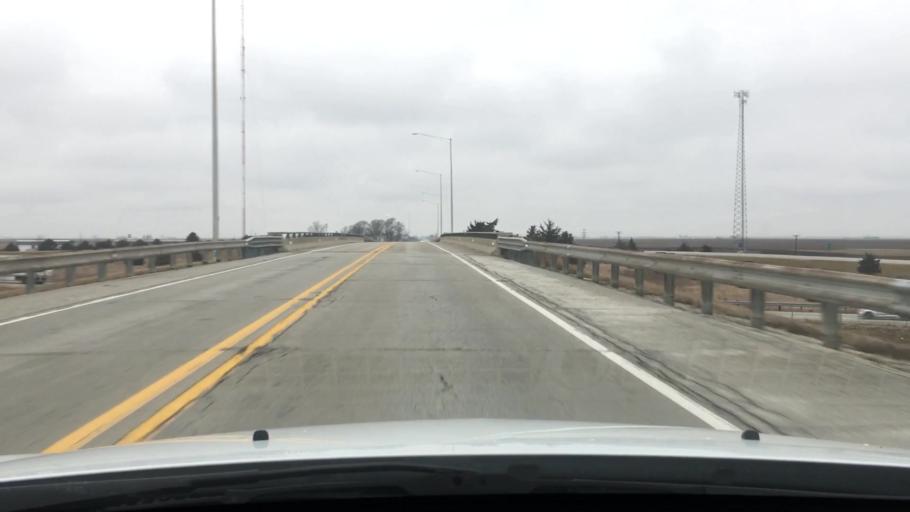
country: US
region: Illinois
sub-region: Iroquois County
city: Clifton
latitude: 40.8841
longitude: -87.9665
